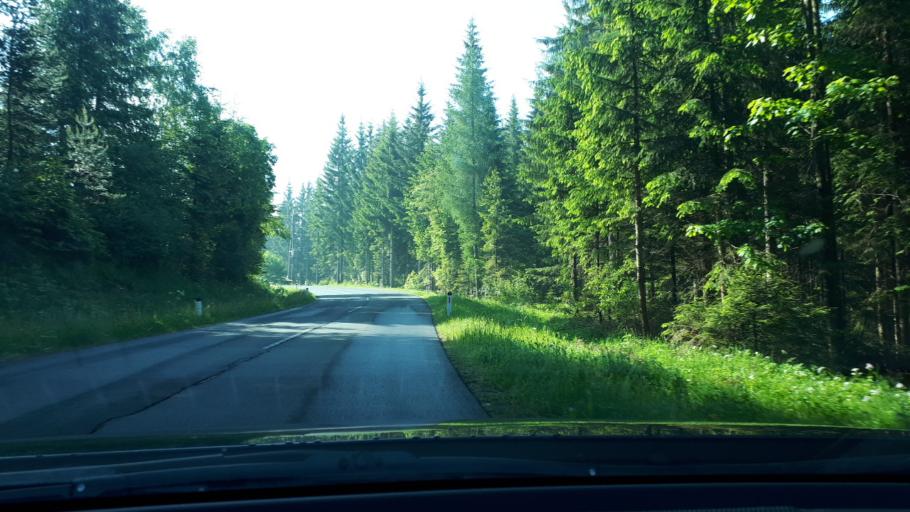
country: AT
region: Carinthia
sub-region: Politischer Bezirk Wolfsberg
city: Preitenegg
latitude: 46.9348
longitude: 14.9669
